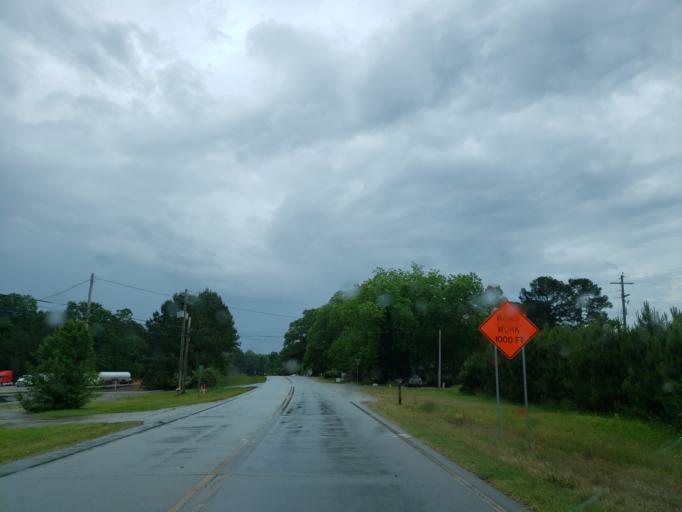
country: US
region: Georgia
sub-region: Haralson County
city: Buchanan
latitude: 33.7898
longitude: -85.1801
